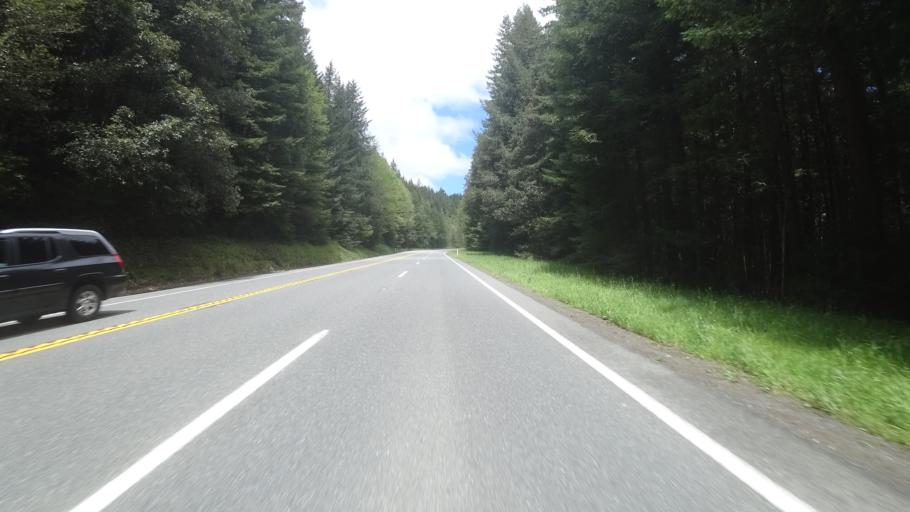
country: US
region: California
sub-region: Humboldt County
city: Blue Lake
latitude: 40.9312
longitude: -123.9000
